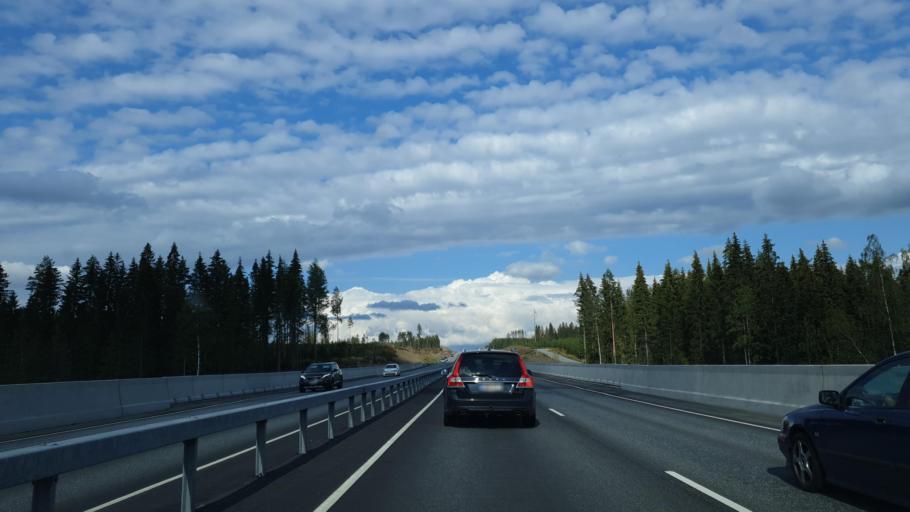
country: FI
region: Southern Savonia
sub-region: Pieksaemaeki
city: Juva
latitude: 61.8200
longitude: 27.6213
